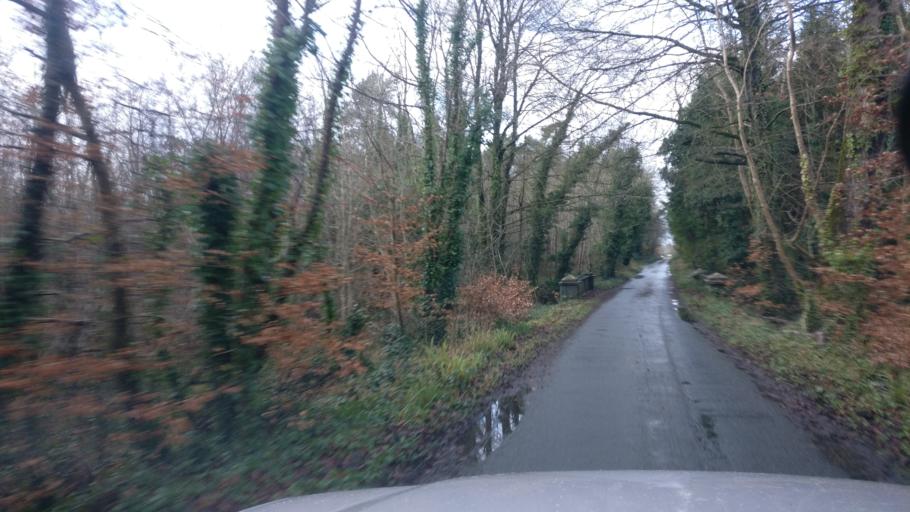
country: IE
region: Connaught
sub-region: County Galway
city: Loughrea
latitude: 53.2433
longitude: -8.6559
